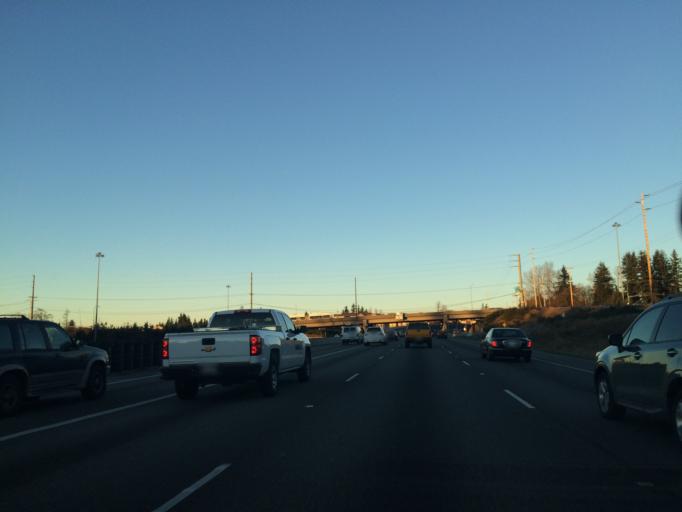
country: US
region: Washington
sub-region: Snohomish County
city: Martha Lake
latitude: 47.8475
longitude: -122.2578
